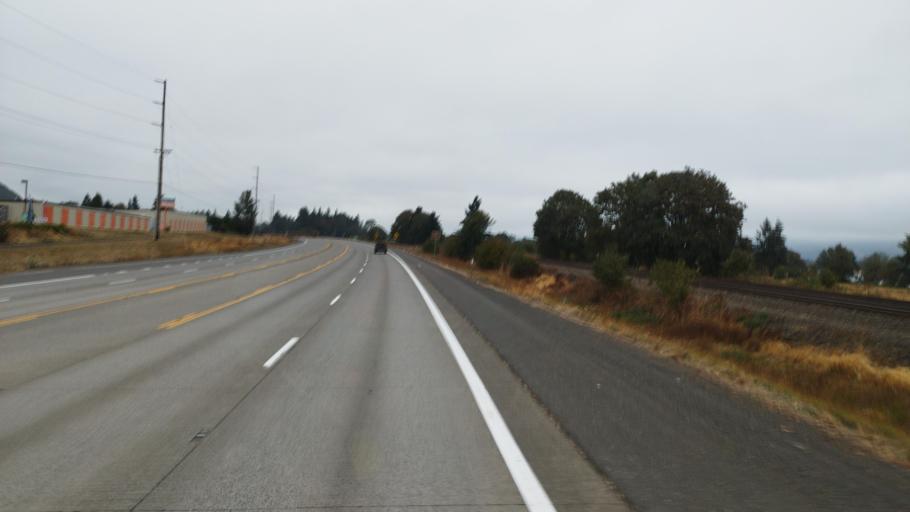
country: US
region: Oregon
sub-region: Columbia County
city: Columbia City
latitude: 45.8971
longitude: -122.8128
